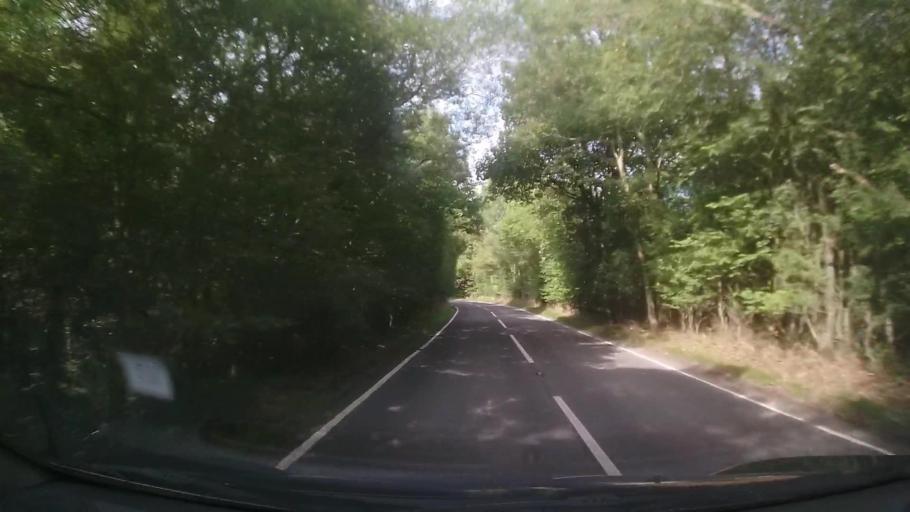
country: GB
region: England
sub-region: Shropshire
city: Lydham
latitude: 52.5576
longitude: -2.9975
